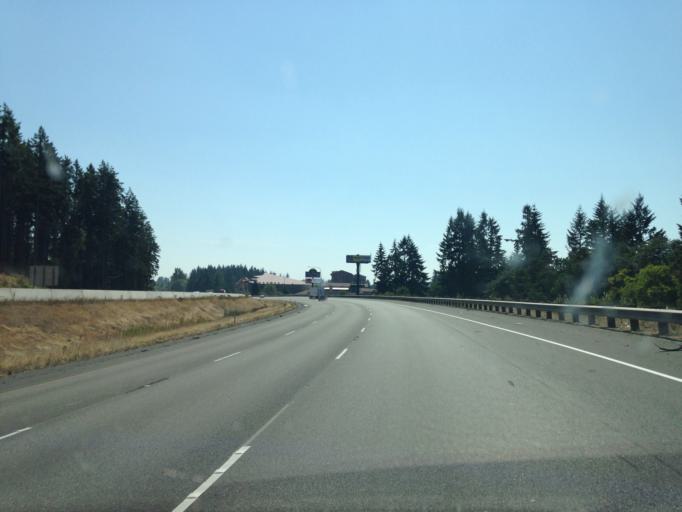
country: US
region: Washington
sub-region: Thurston County
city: Grand Mound
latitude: 46.7963
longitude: -123.0107
